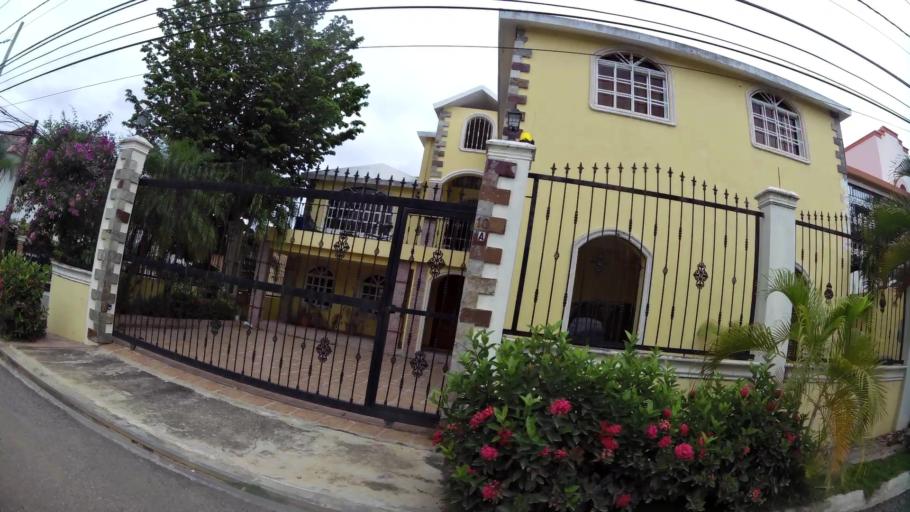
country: DO
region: Santiago
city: Santiago de los Caballeros
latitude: 19.4323
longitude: -70.6627
